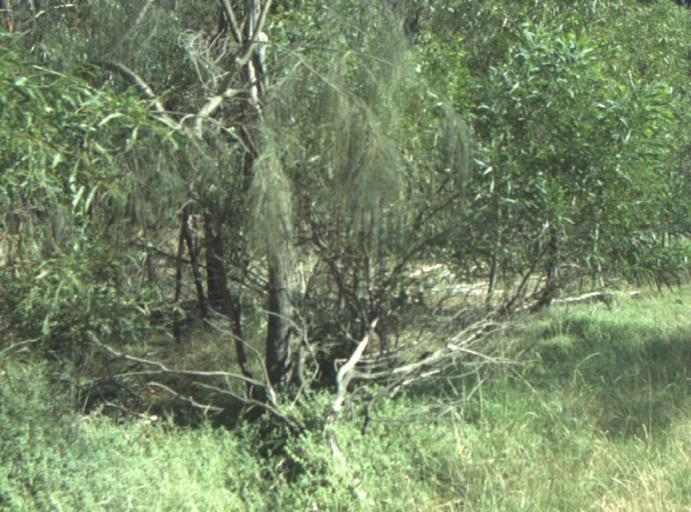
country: AU
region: Victoria
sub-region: Greater Geelong
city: Lara
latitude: -37.9385
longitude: 144.3931
